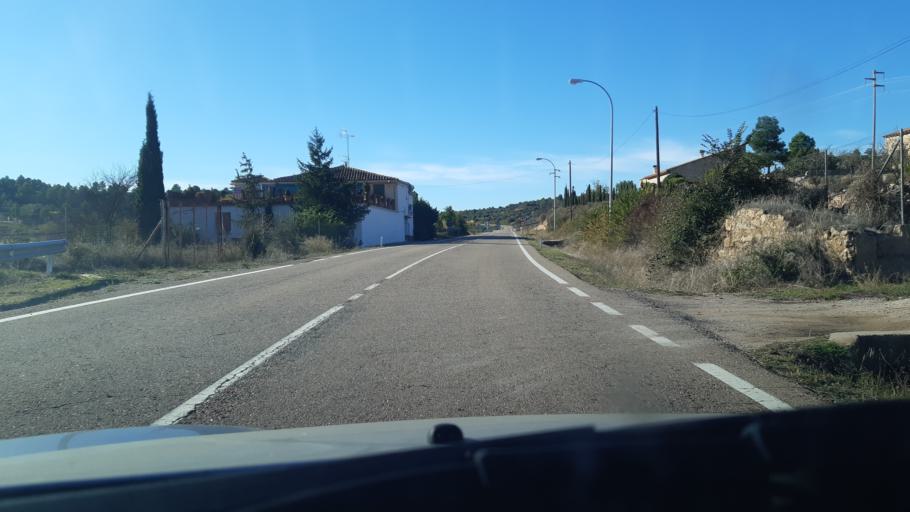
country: ES
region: Aragon
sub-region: Provincia de Teruel
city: Valjunquera
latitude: 40.9520
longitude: 0.0222
